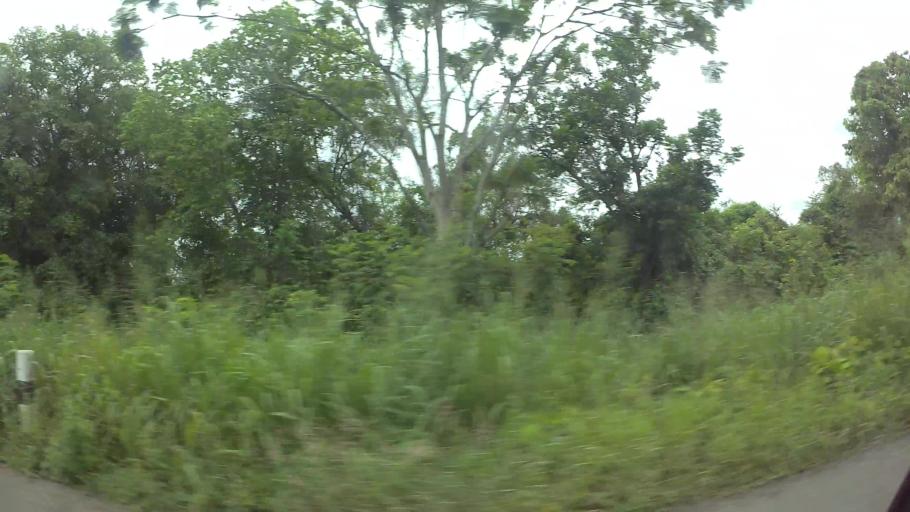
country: TH
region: Chon Buri
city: Si Racha
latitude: 13.1822
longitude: 100.9719
